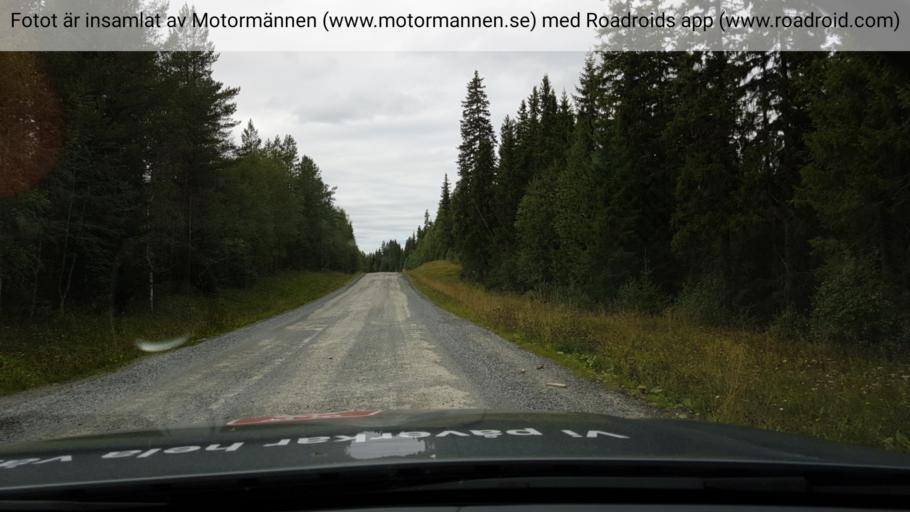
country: SE
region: Jaemtland
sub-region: Krokoms Kommun
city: Valla
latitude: 63.6478
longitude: 13.8151
